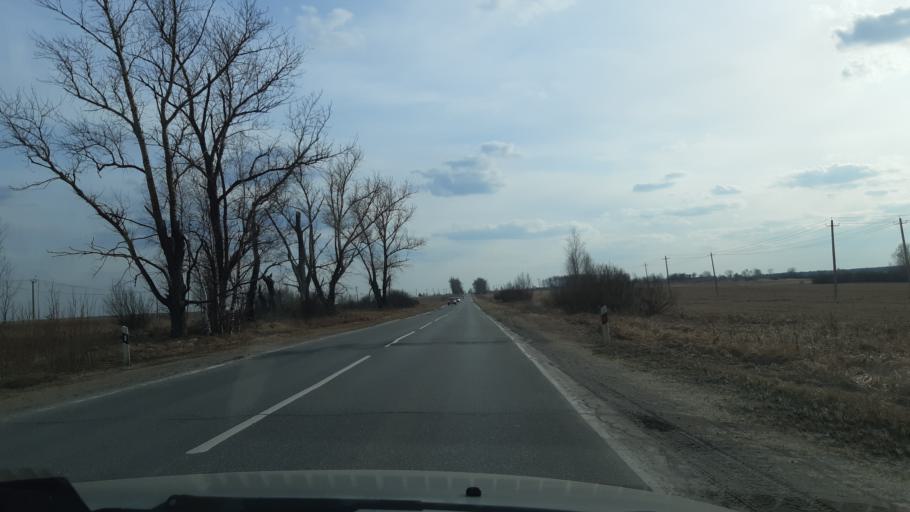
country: RU
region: Vladimir
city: Nikologory
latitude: 56.1720
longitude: 42.0015
